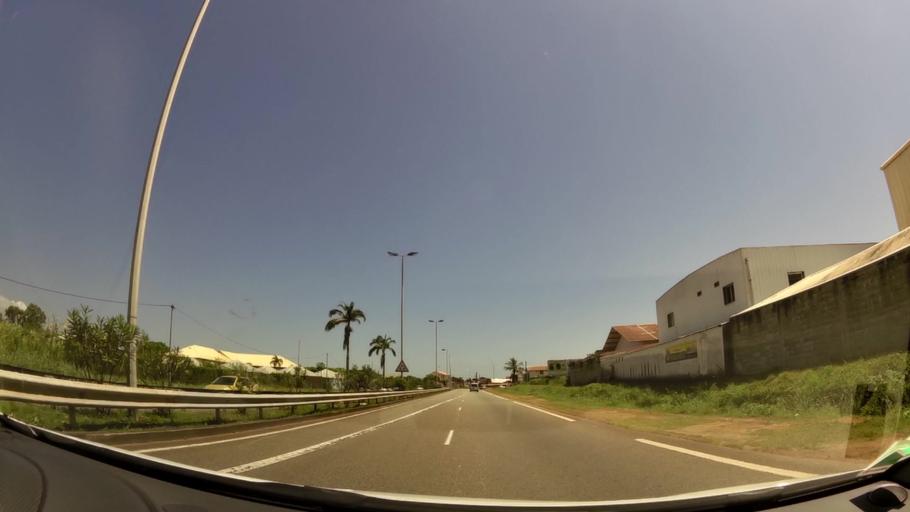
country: GF
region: Guyane
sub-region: Guyane
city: Cayenne
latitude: 4.9299
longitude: -52.3294
